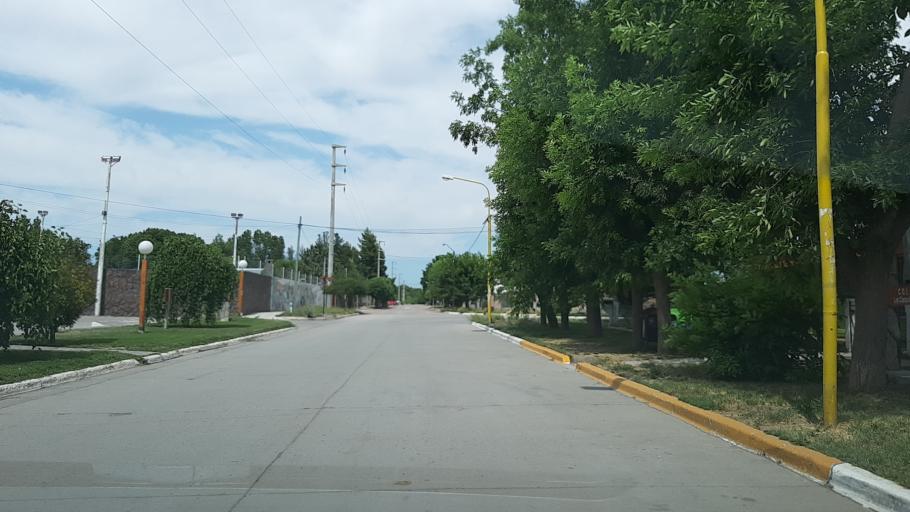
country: AR
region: Neuquen
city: Piedra del Aguila
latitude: -40.0505
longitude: -70.0747
